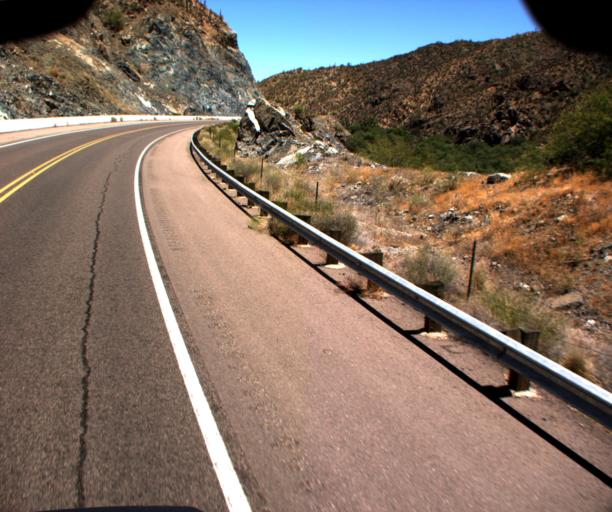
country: US
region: Arizona
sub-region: Pinal County
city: Kearny
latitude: 33.0704
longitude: -110.7259
